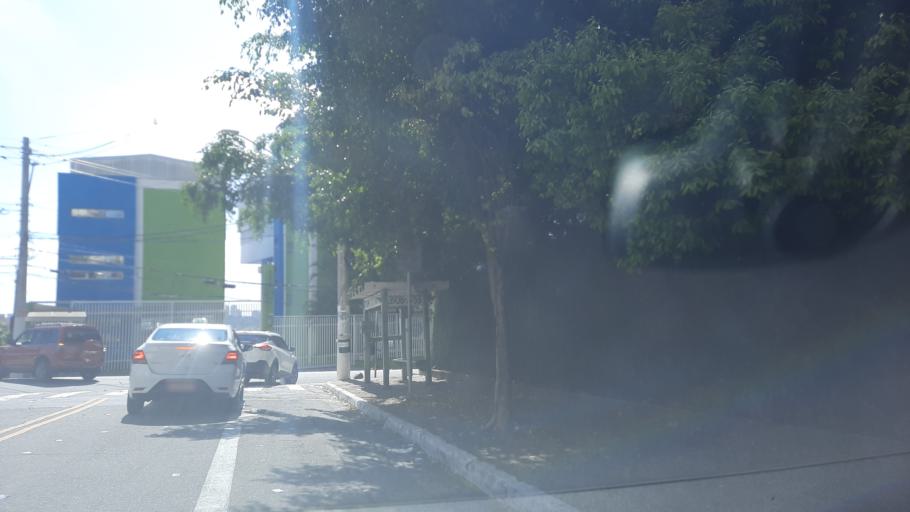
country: BR
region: Sao Paulo
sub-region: Sao Paulo
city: Sao Paulo
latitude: -23.4994
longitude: -46.6754
